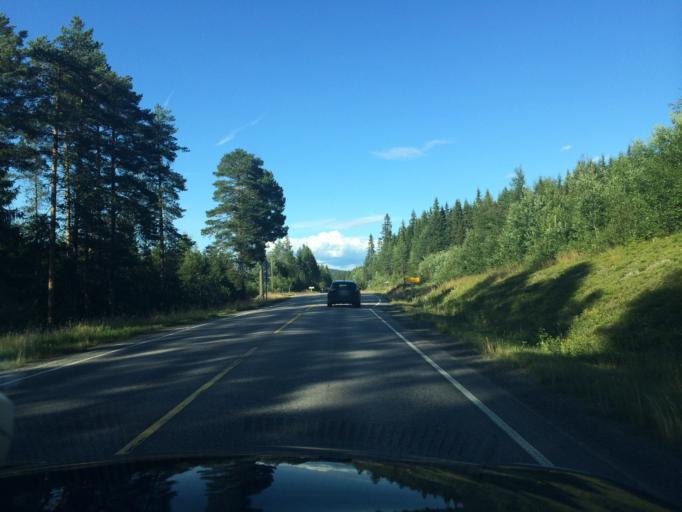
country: NO
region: Hedmark
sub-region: Elverum
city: Elverum
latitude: 60.9667
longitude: 11.7195
